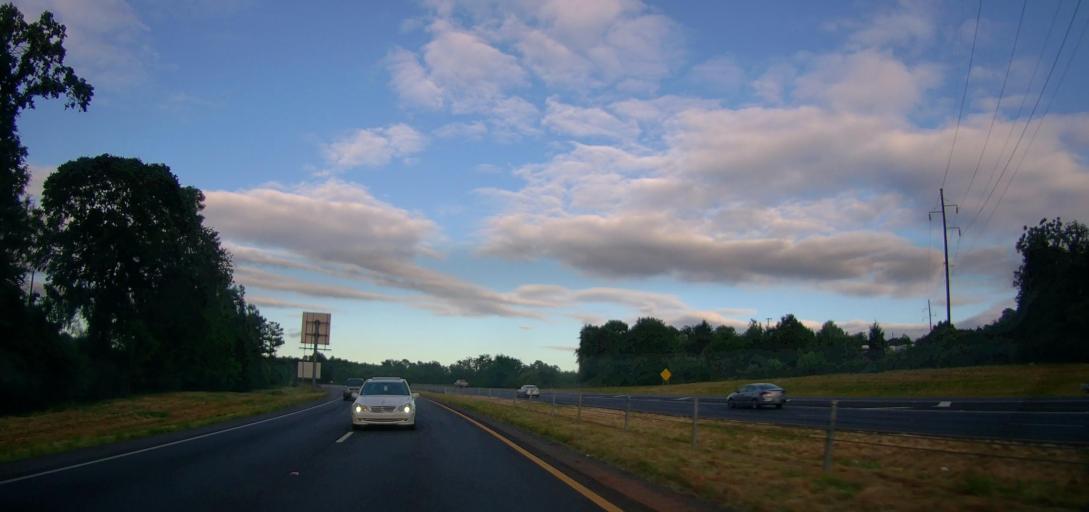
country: US
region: Georgia
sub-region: Clarke County
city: Country Club Estates
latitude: 33.9707
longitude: -83.4042
